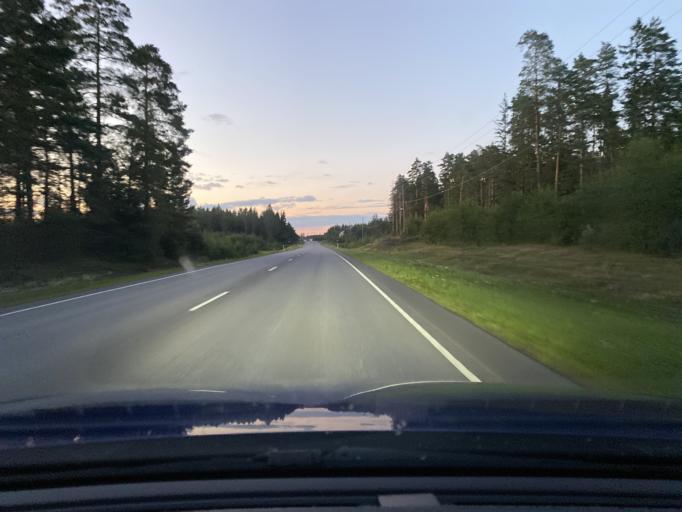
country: FI
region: Varsinais-Suomi
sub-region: Loimaa
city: Poeytyae
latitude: 60.7406
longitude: 22.5995
